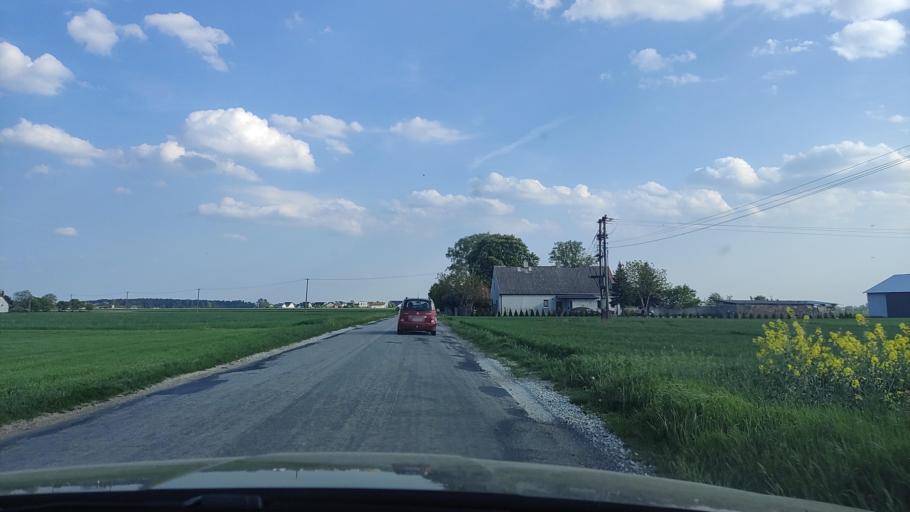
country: PL
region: Greater Poland Voivodeship
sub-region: Powiat poznanski
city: Kleszczewo
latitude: 52.3643
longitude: 17.1686
